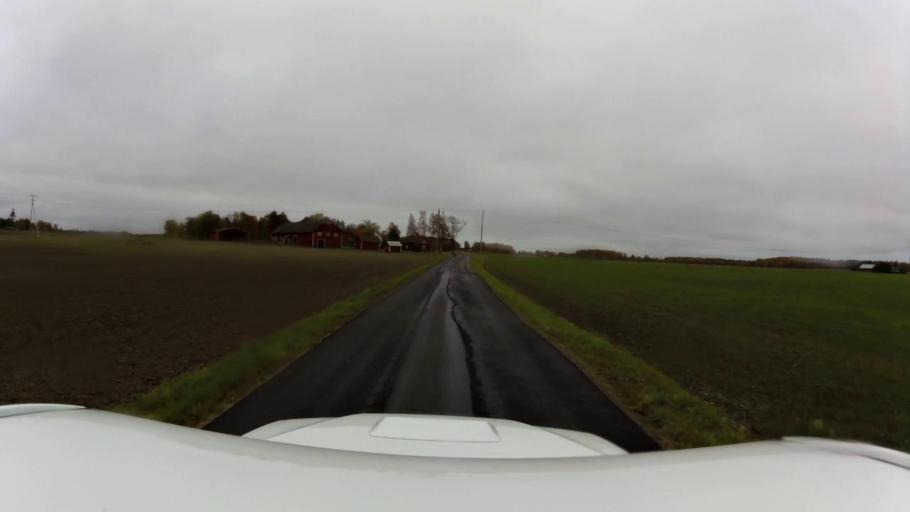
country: SE
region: OEstergoetland
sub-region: Linkopings Kommun
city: Ekangen
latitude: 58.4558
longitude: 15.7043
